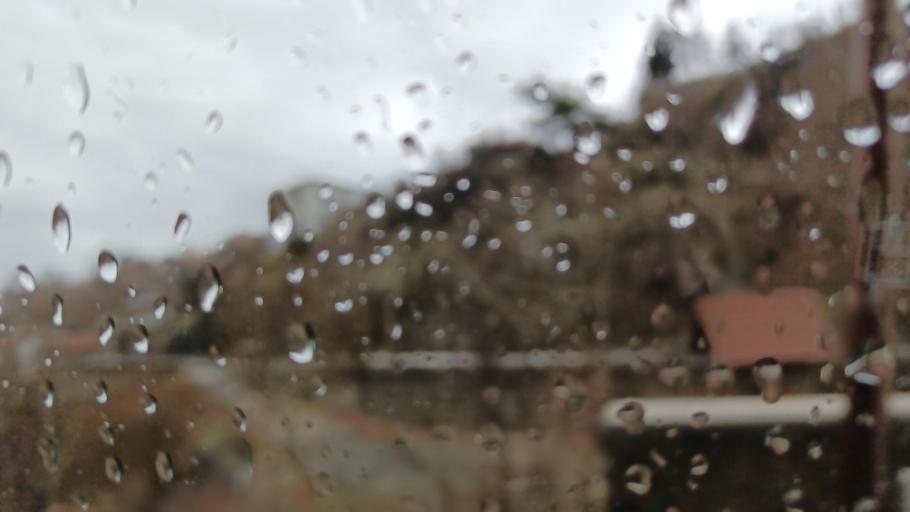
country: CY
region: Limassol
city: Kyperounta
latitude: 34.9420
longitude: 32.9733
